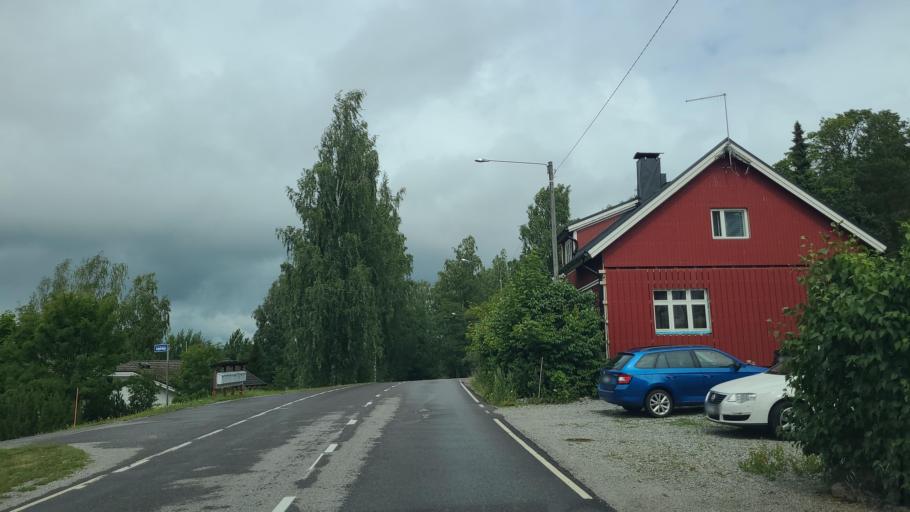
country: FI
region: Varsinais-Suomi
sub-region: Turku
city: Sauvo
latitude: 60.3376
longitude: 22.7045
